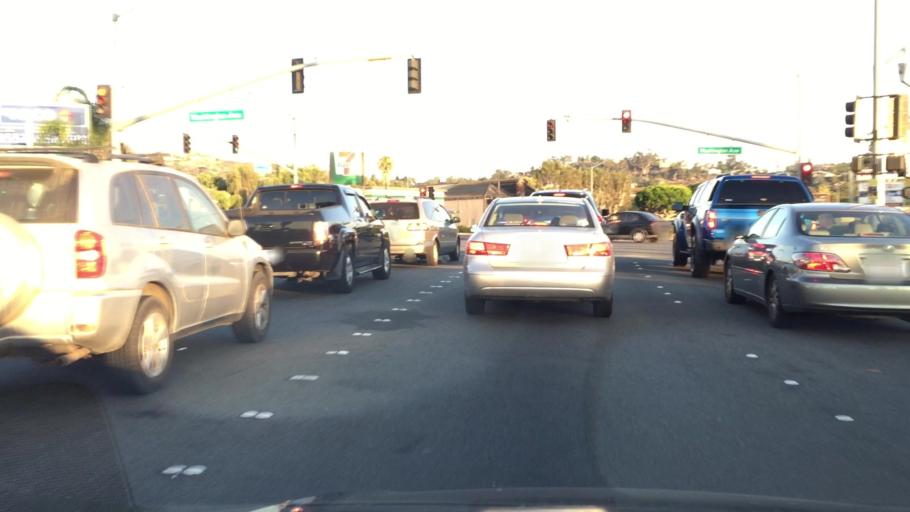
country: US
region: California
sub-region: San Diego County
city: Bostonia
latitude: 32.7880
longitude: -116.9284
